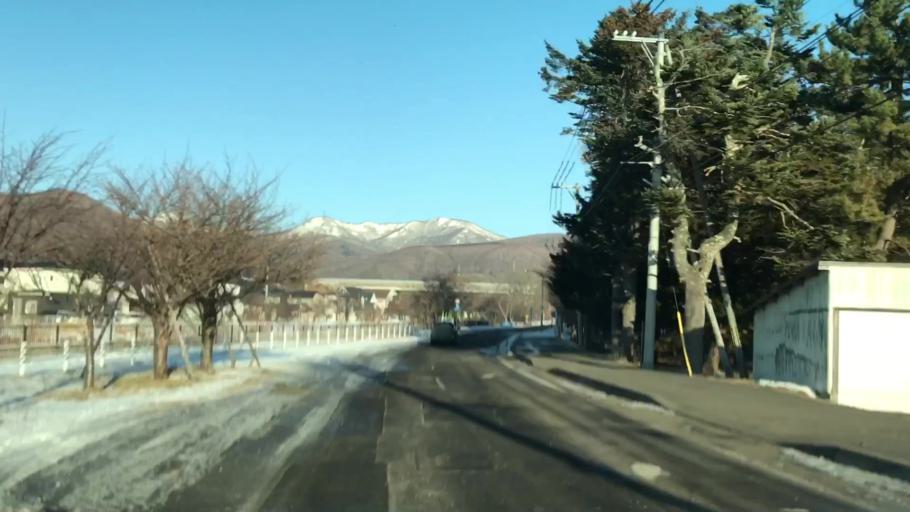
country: JP
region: Hokkaido
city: Muroran
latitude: 42.3870
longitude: 141.0698
